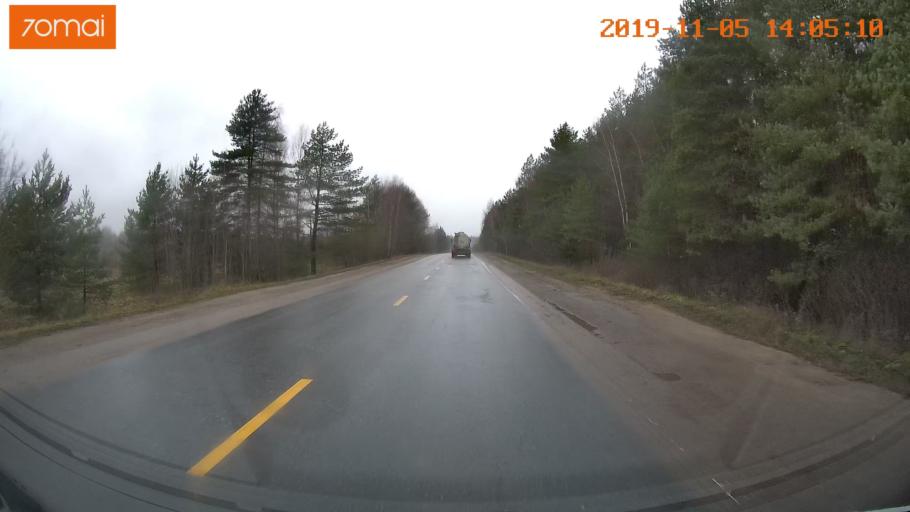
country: RU
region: Ivanovo
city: Kokhma
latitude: 56.9976
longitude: 41.1627
